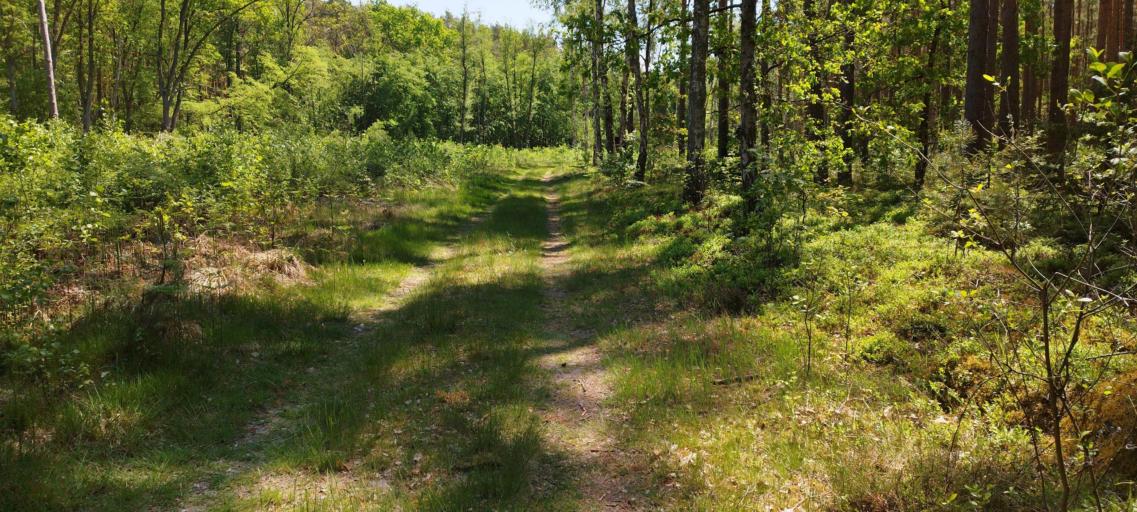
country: DE
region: Brandenburg
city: Rauen
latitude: 52.3871
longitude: 13.9924
